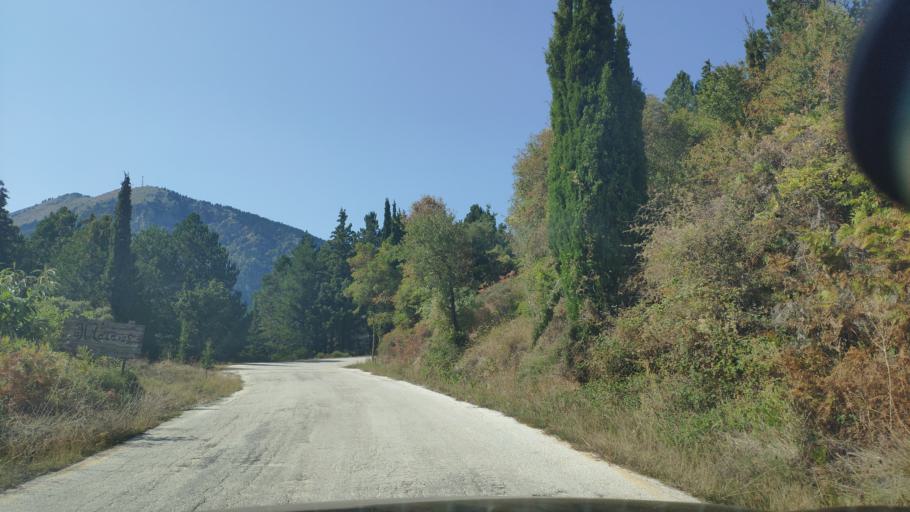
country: GR
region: Peloponnese
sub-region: Nomos Korinthias
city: Nemea
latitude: 37.8674
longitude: 22.3866
